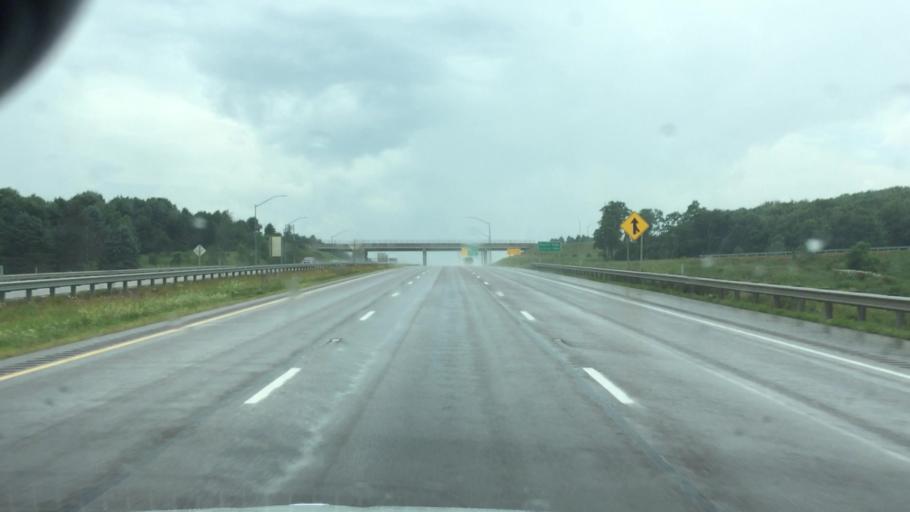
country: US
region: Pennsylvania
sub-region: Somerset County
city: Meyersdale
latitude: 39.6874
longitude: -79.2461
